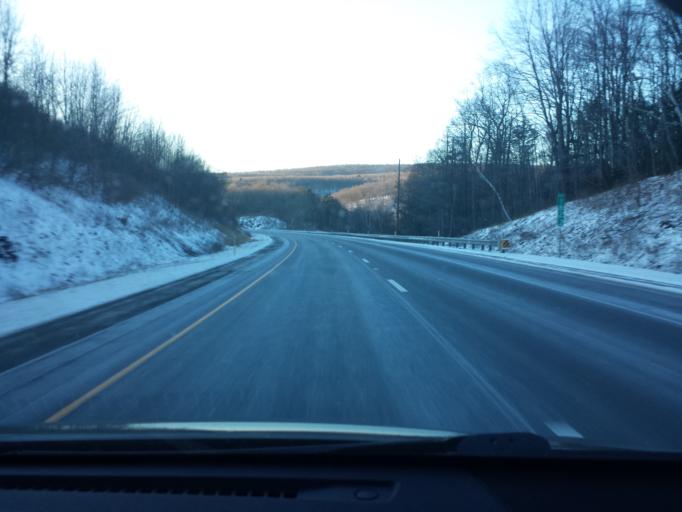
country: US
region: Pennsylvania
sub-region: Clinton County
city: Castanea
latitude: 41.0609
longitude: -77.3640
